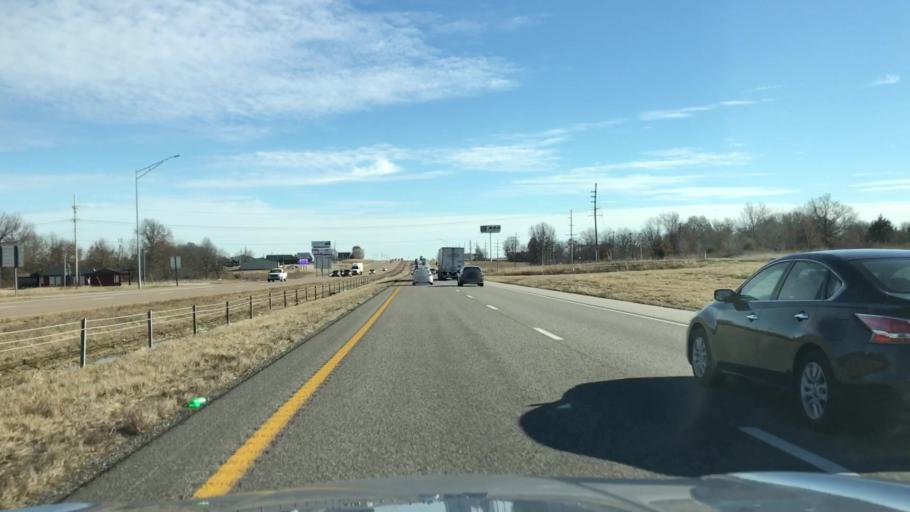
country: US
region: Missouri
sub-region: Montgomery County
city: Montgomery City
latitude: 38.8989
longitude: -91.4542
